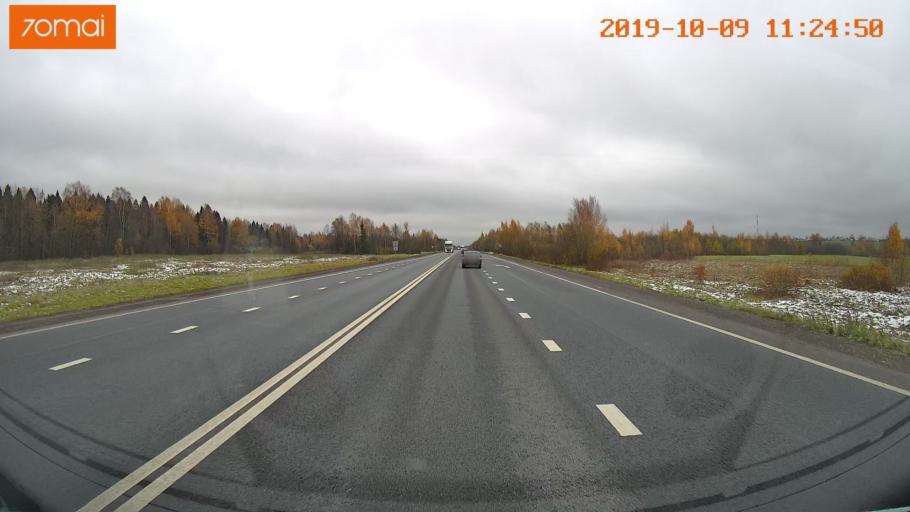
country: RU
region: Vologda
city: Vologda
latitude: 59.1075
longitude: 39.9844
